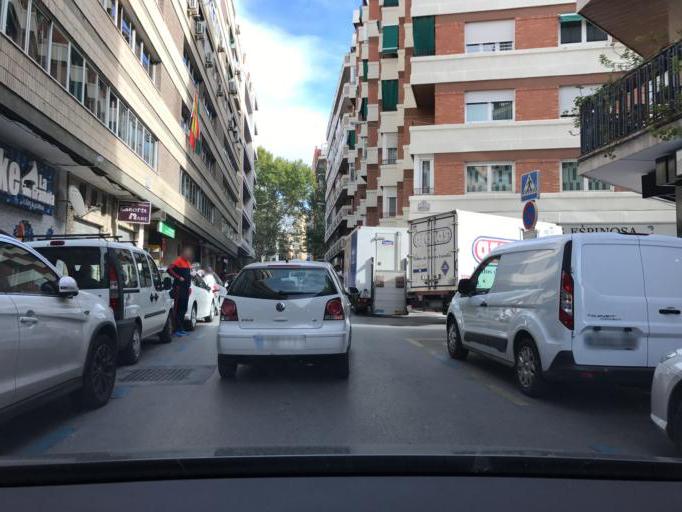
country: ES
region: Andalusia
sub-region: Provincia de Granada
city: Granada
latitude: 37.1718
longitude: -3.6054
